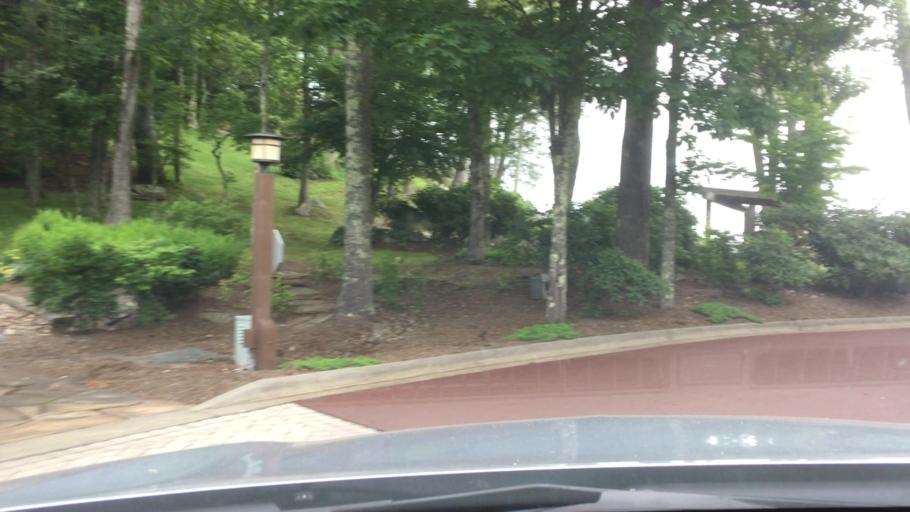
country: US
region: North Carolina
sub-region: Yancey County
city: Burnsville
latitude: 35.8709
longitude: -82.3469
